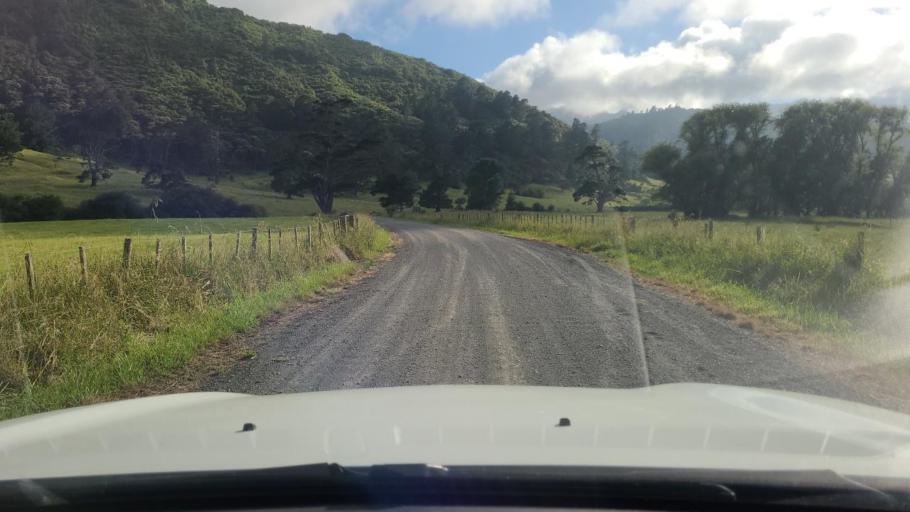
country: NZ
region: Bay of Plenty
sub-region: Western Bay of Plenty District
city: Katikati
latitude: -37.5629
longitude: 175.7437
